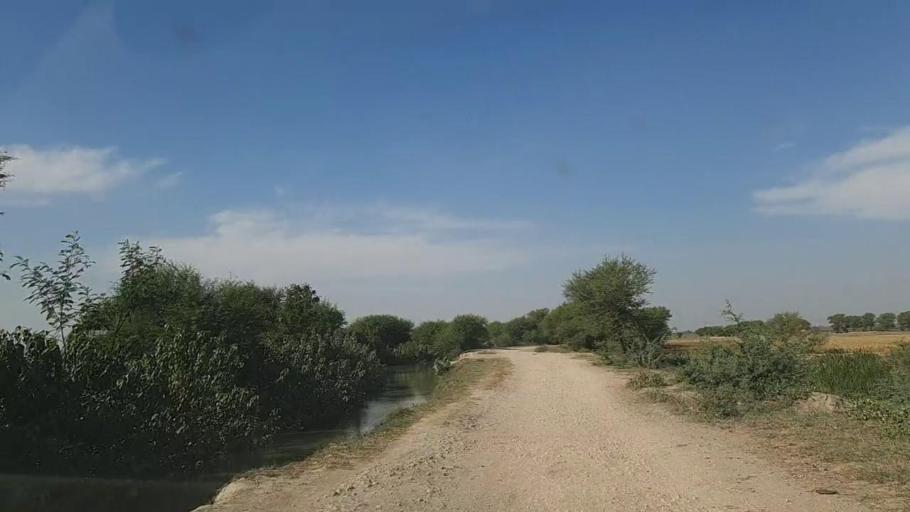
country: PK
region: Sindh
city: Bulri
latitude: 24.8646
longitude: 68.2676
